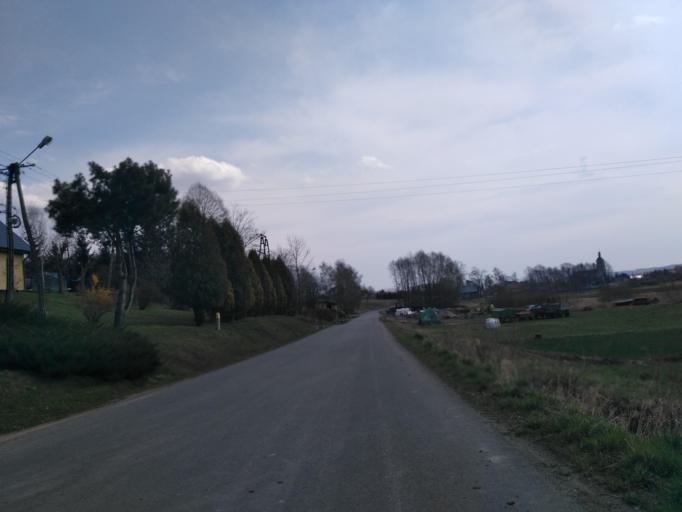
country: PL
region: Subcarpathian Voivodeship
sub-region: Powiat ropczycko-sedziszowski
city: Iwierzyce
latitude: 50.0320
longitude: 21.7601
